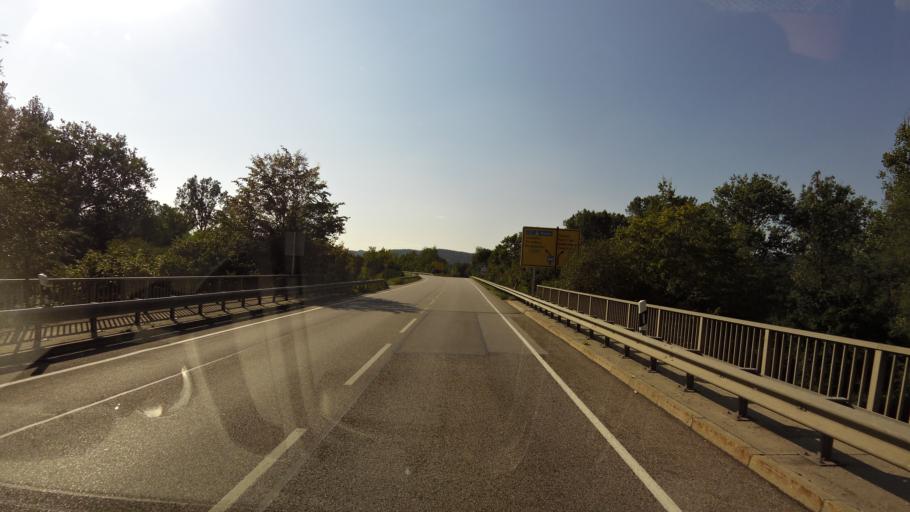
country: DE
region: Bavaria
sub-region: Lower Bavaria
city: Simbach am Inn
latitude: 48.2503
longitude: 13.0081
